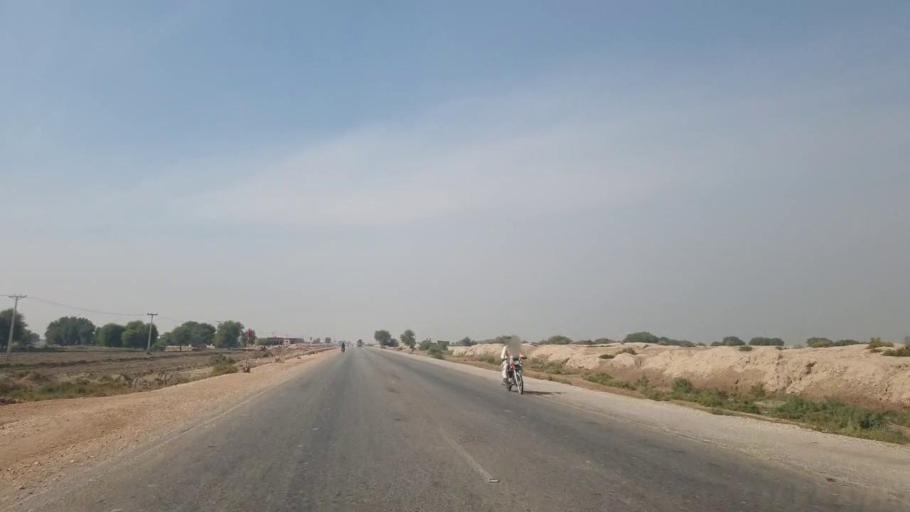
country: PK
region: Sindh
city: Sann
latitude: 25.9882
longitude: 68.1788
